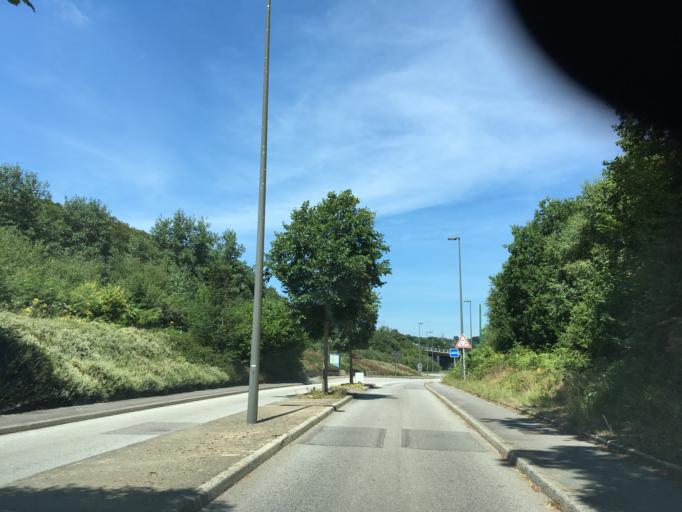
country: FR
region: Brittany
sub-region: Departement du Finistere
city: Quimper
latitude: 48.0109
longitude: -4.1206
